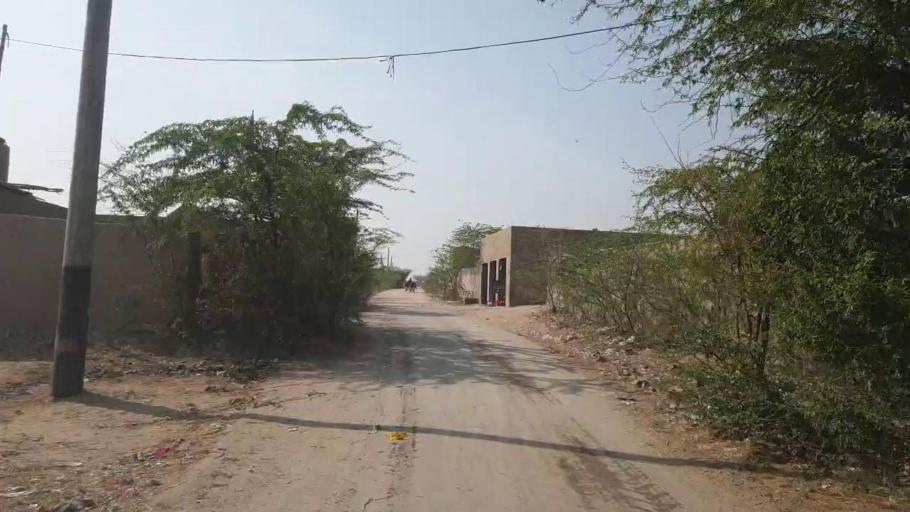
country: PK
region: Sindh
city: Umarkot
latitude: 25.3312
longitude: 69.7348
